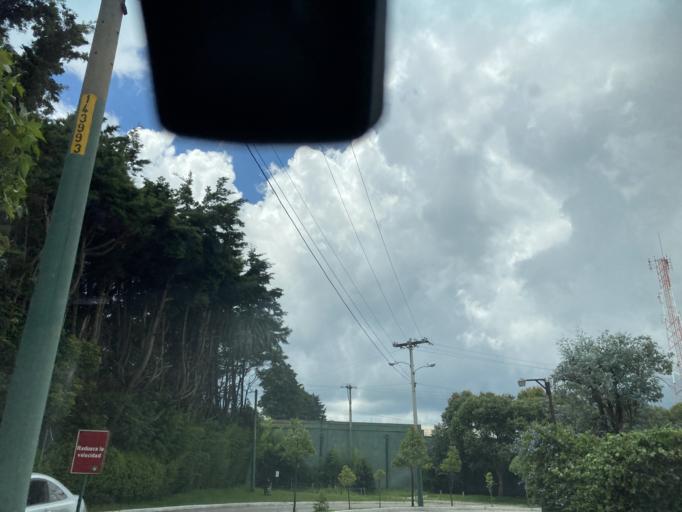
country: GT
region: Guatemala
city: San Jose Pinula
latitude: 14.5421
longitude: -90.4293
